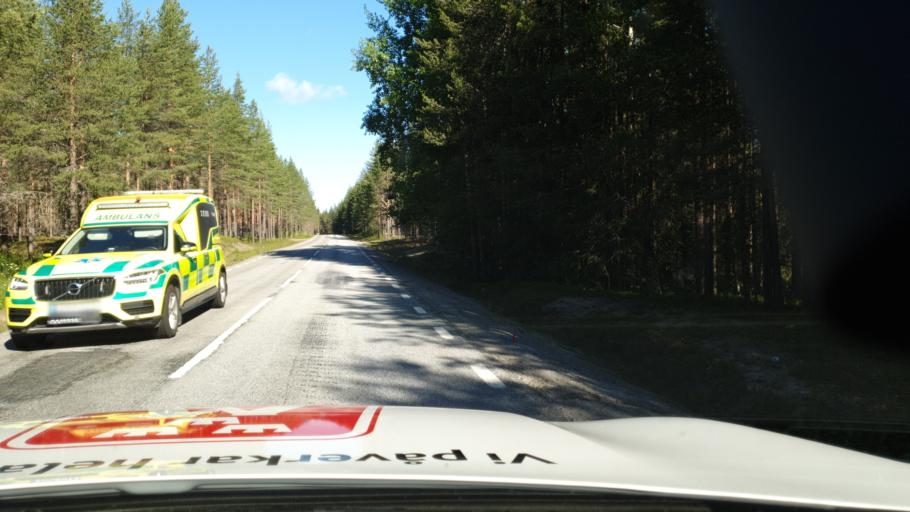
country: SE
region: Vaesterbotten
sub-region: Vindelns Kommun
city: Vindeln
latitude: 64.2394
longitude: 19.6921
